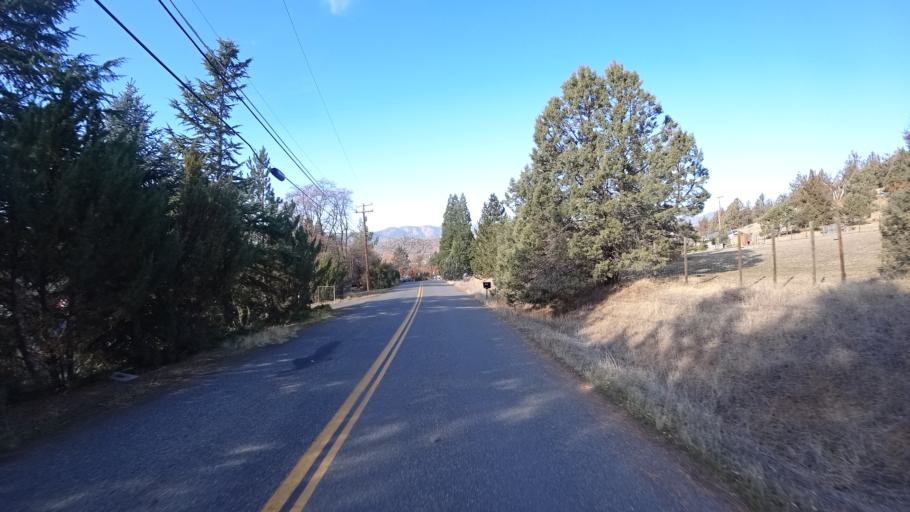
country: US
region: California
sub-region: Siskiyou County
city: Yreka
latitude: 41.6997
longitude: -122.6333
